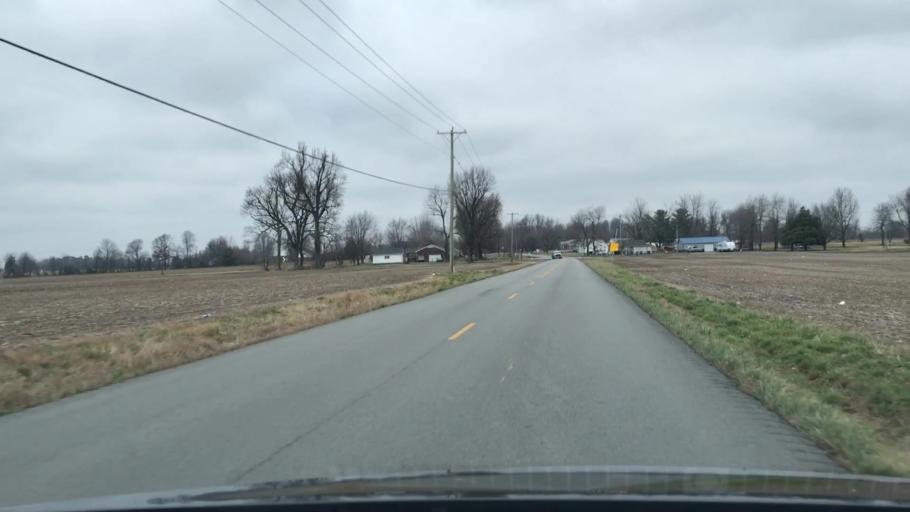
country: US
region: Kentucky
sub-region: Muhlenberg County
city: Morehead
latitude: 37.3546
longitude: -87.2287
